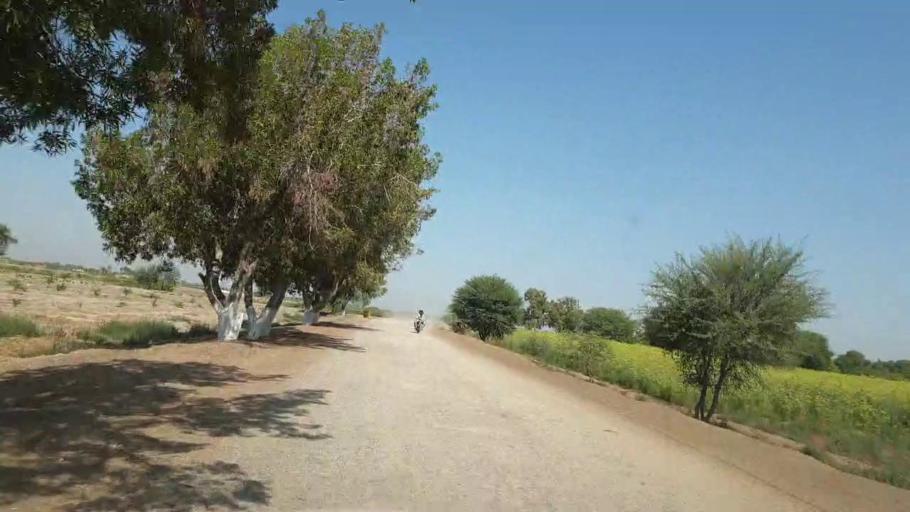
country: PK
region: Sindh
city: Kunri
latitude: 25.1354
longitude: 69.5094
